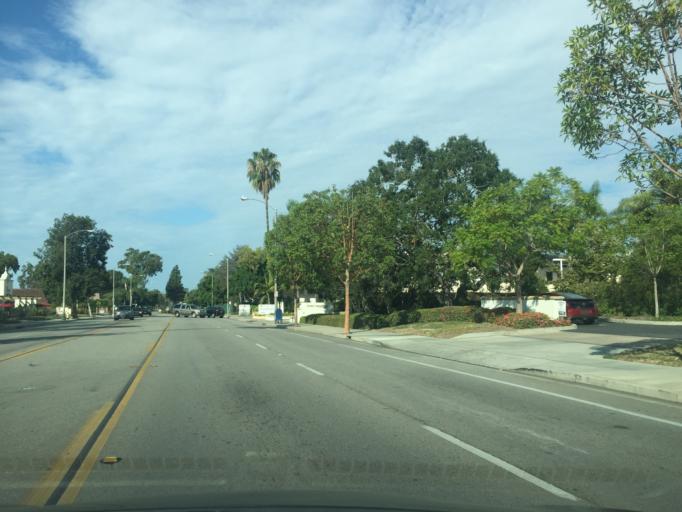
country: US
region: California
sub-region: Santa Barbara County
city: Mission Canyon
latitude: 34.4404
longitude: -119.7418
